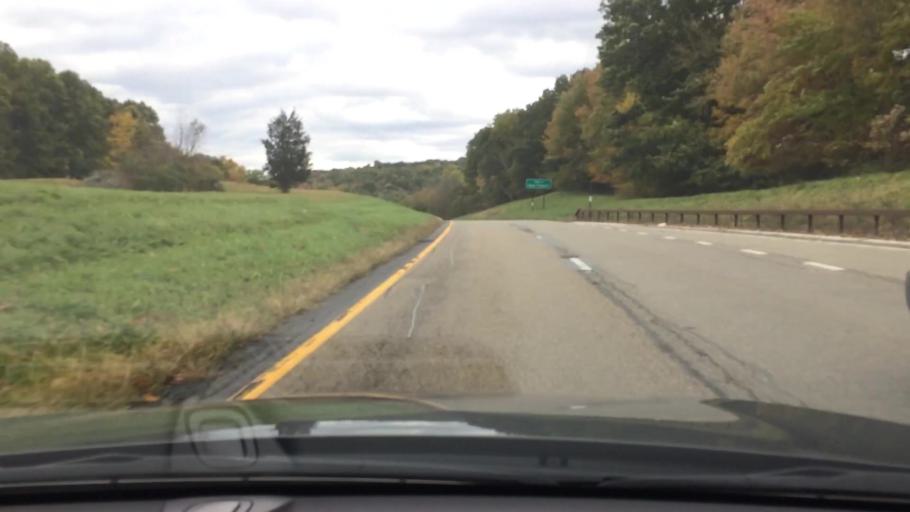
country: US
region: New York
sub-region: Dutchess County
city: Hillside Lake
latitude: 41.6293
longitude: -73.7807
